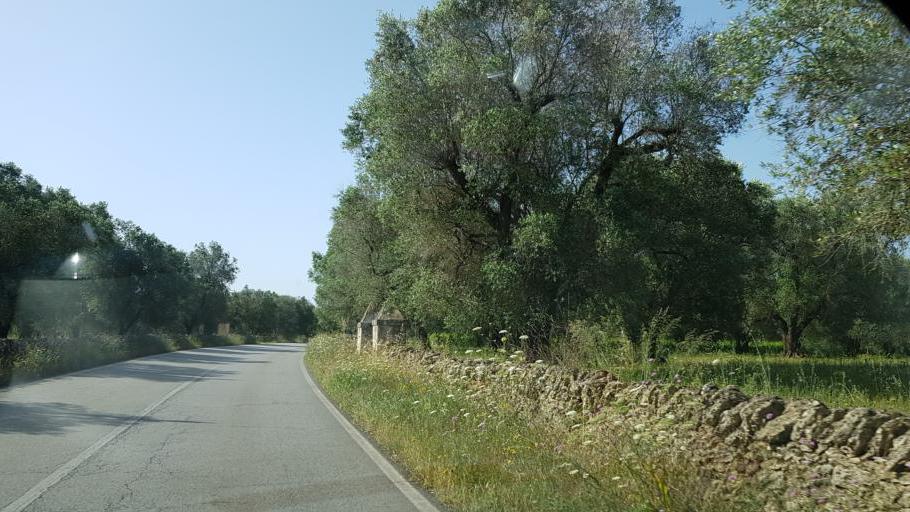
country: IT
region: Apulia
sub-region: Provincia di Brindisi
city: Mesagne
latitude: 40.5172
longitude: 17.8254
